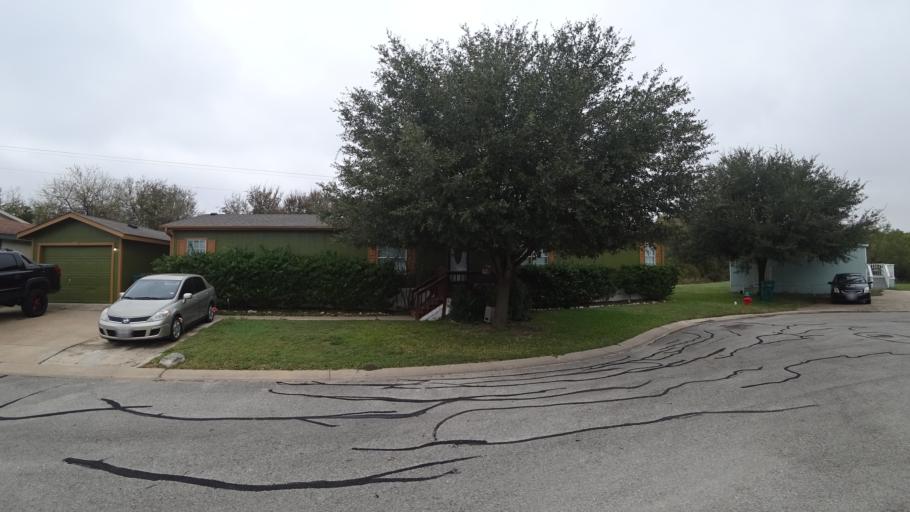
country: US
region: Texas
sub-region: Travis County
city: Pflugerville
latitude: 30.4183
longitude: -97.6060
